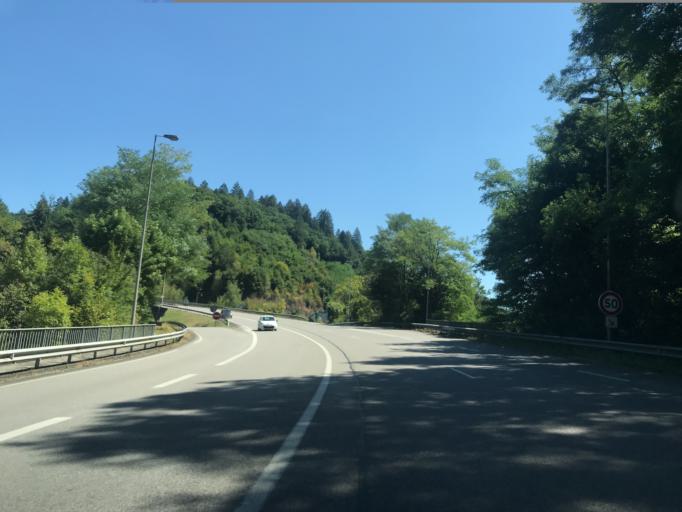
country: FR
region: Limousin
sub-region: Departement de la Correze
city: Laguenne
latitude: 45.2479
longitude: 1.7681
